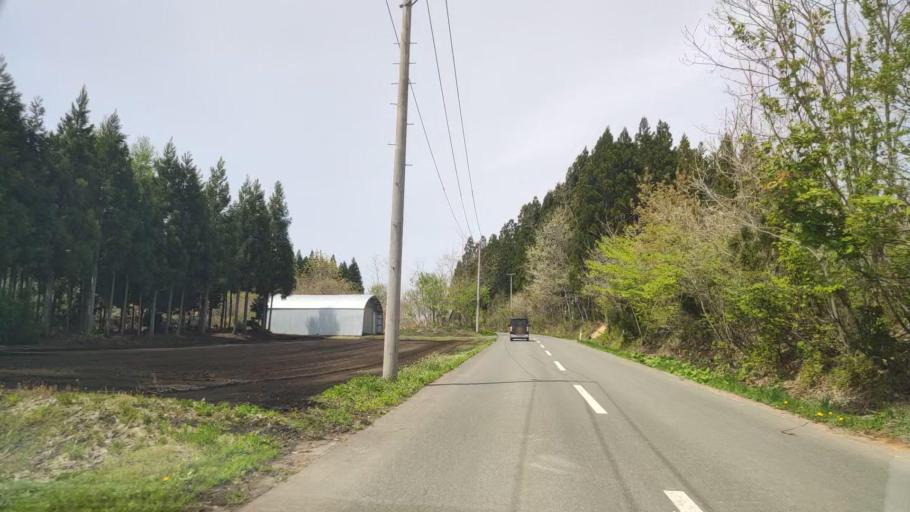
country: JP
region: Aomori
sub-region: Misawa Shi
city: Inuotose
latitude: 40.7729
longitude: 141.1227
